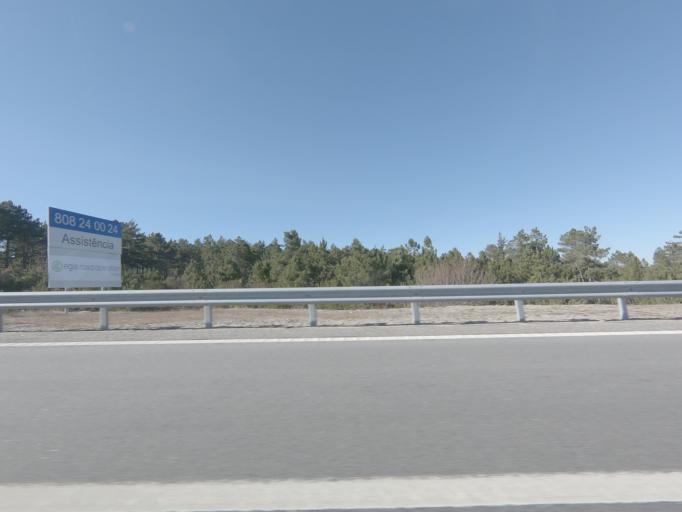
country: PT
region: Vila Real
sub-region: Vila Pouca de Aguiar
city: Vila Pouca de Aguiar
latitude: 41.5161
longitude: -7.6553
